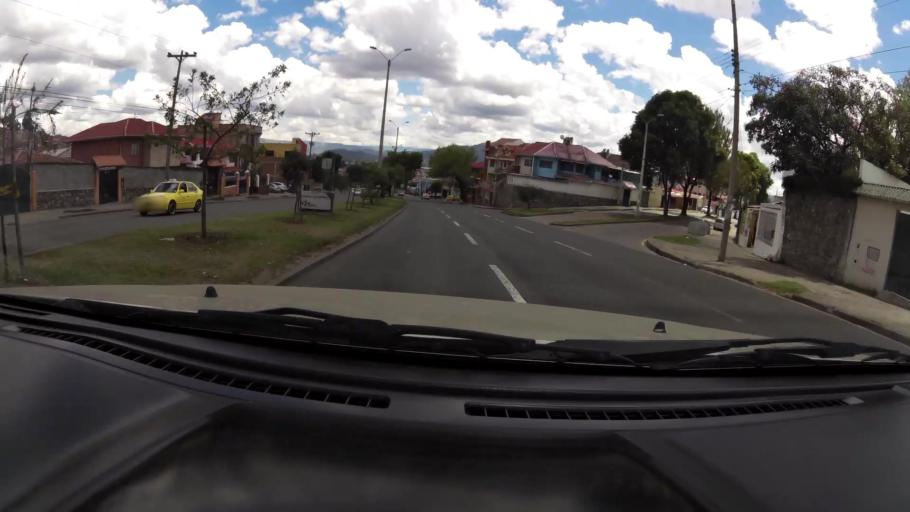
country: EC
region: Azuay
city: Cuenca
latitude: -2.8861
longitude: -78.9956
